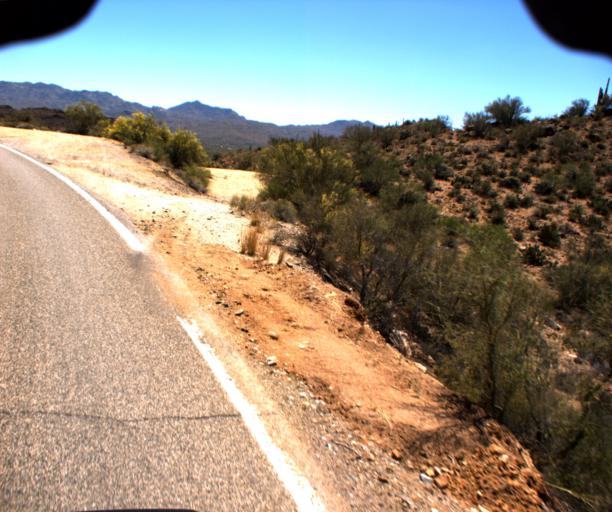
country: US
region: Arizona
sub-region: Yavapai County
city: Bagdad
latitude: 34.5078
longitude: -113.0748
